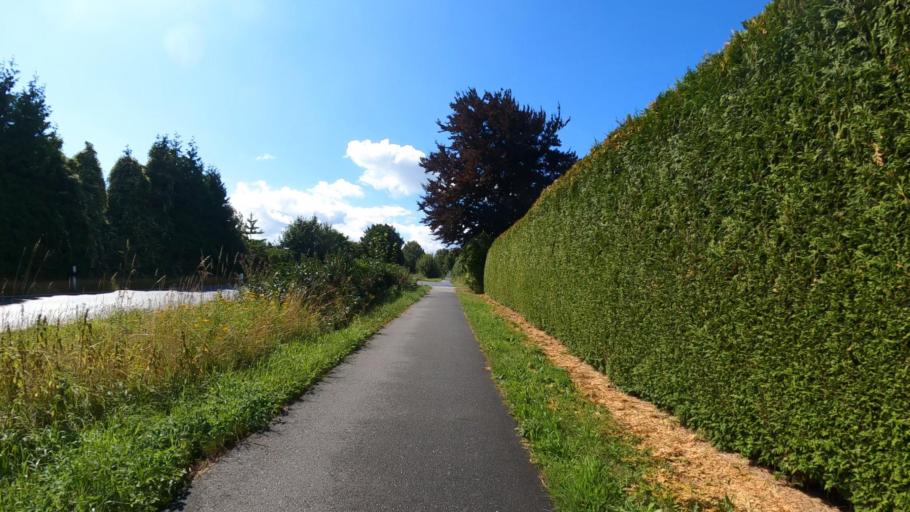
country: DE
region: Schleswig-Holstein
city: Fuhlendorf
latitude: 53.9411
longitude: 9.8952
